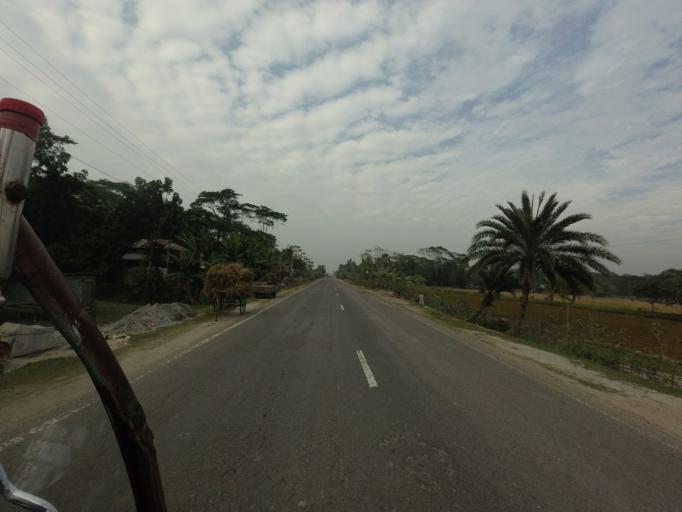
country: BD
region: Barisal
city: Nalchiti
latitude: 22.4548
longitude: 90.3408
